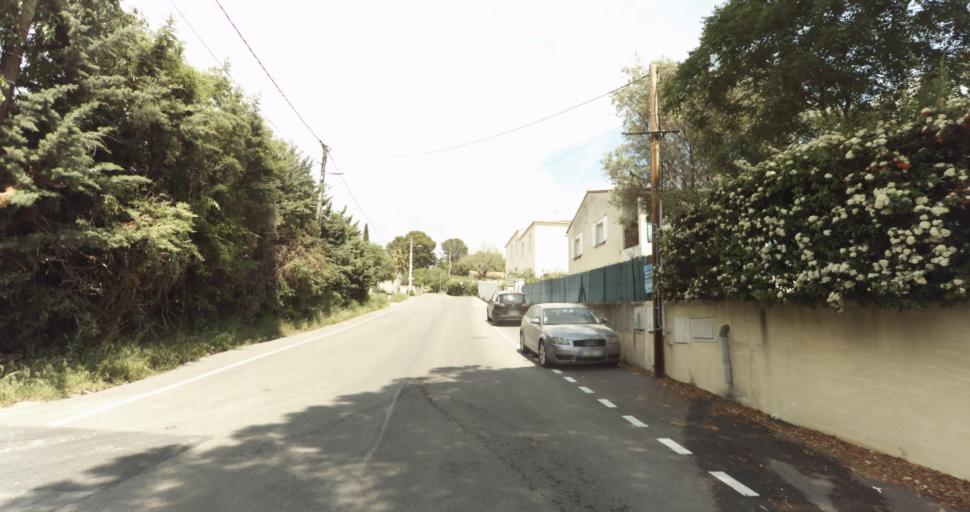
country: FR
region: Languedoc-Roussillon
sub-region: Departement du Gard
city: Nimes
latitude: 43.8526
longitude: 4.3857
